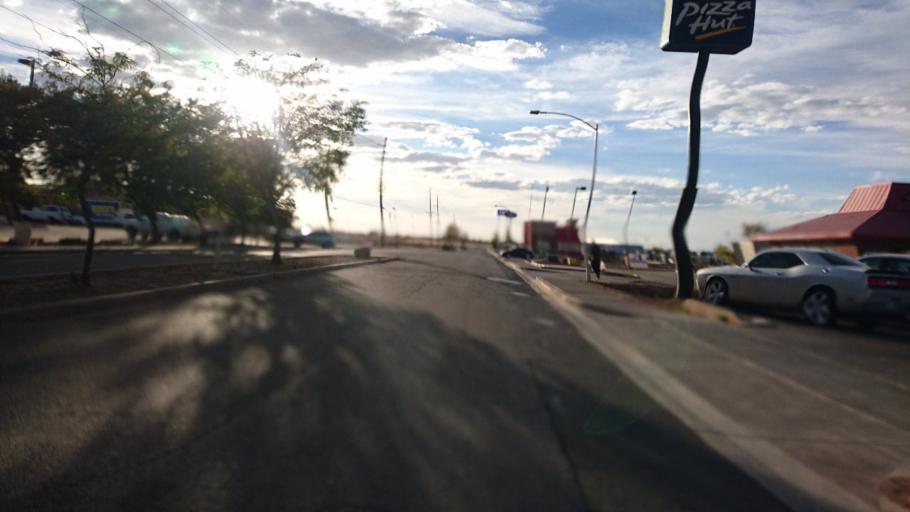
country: US
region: Arizona
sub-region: Navajo County
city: Winslow
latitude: 35.0409
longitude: -110.6998
